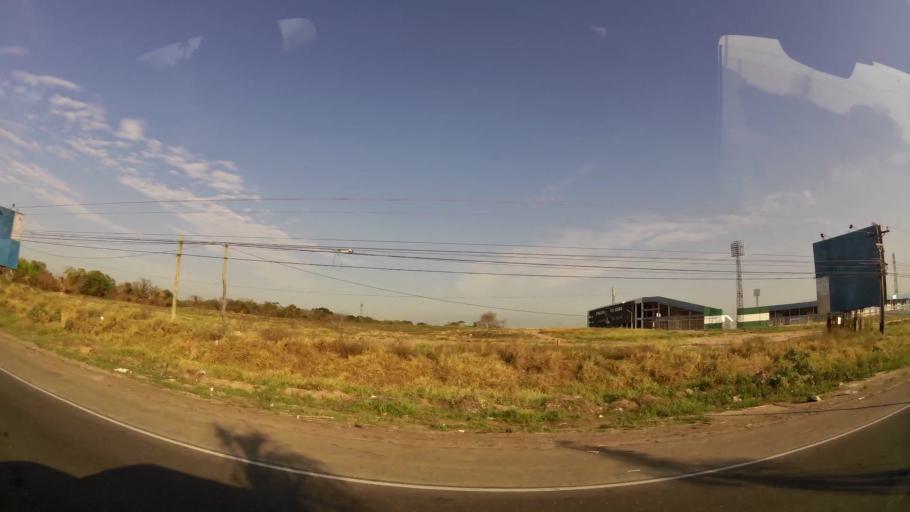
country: BO
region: Santa Cruz
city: Santa Cruz de la Sierra
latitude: -17.6675
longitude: -63.1584
